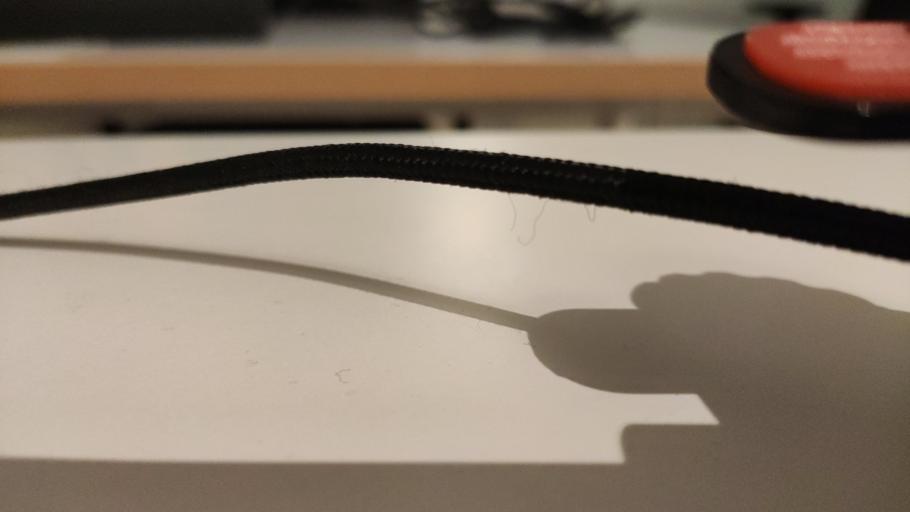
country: RU
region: Moskovskaya
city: Dmitrov
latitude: 56.3638
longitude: 37.5376
